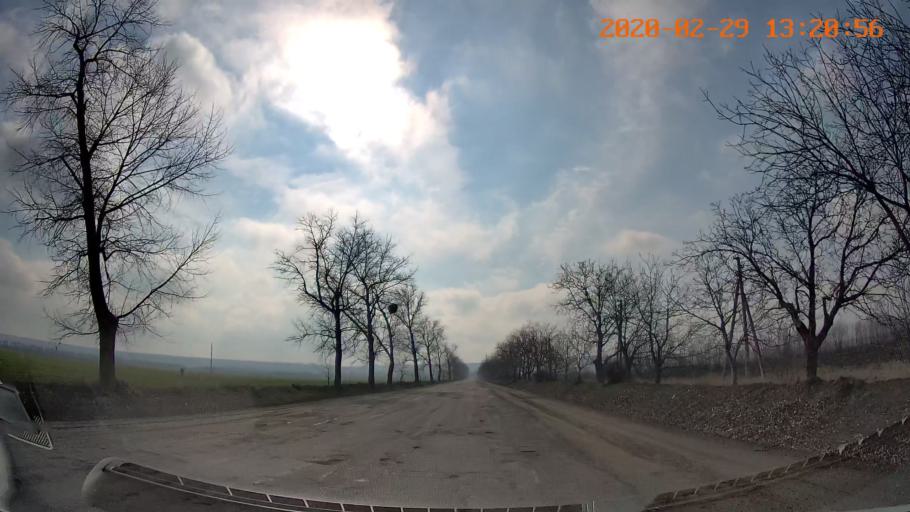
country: MD
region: Telenesti
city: Camenca
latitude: 47.9745
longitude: 28.6371
